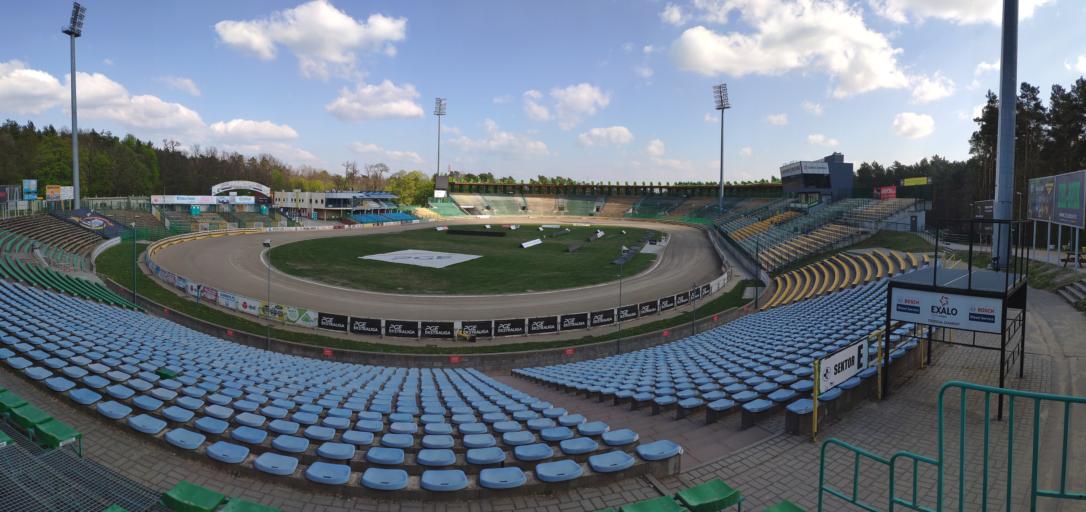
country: PL
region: Lubusz
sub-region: Zielona Gora
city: Zielona Gora
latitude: 51.9294
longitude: 15.5281
